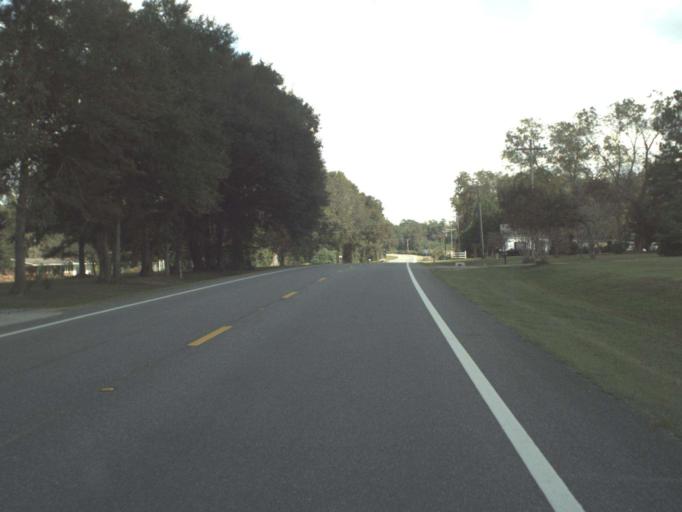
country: US
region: Florida
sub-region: Washington County
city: Chipley
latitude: 30.7952
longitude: -85.5233
